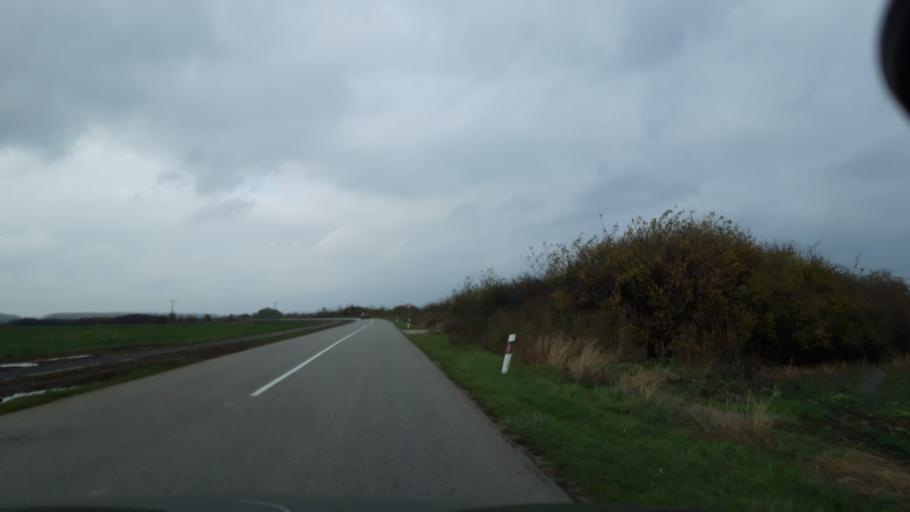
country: RS
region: Autonomna Pokrajina Vojvodina
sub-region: Severnobanatski Okrug
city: Novi Knezevac
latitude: 46.1022
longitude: 20.1073
